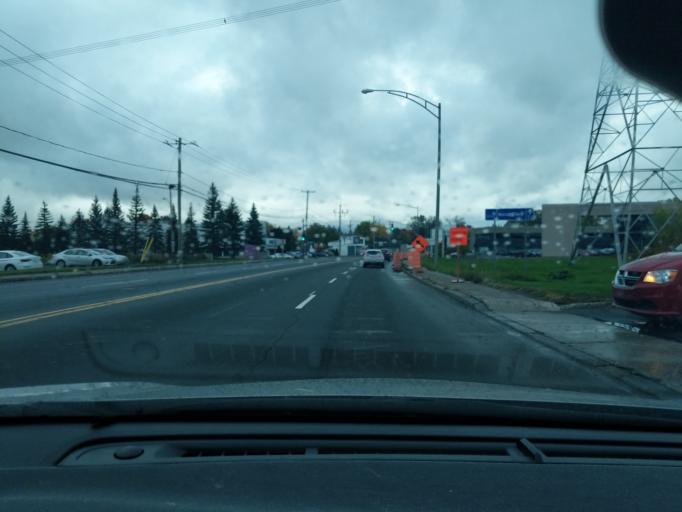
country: CA
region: Quebec
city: L'Ancienne-Lorette
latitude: 46.8054
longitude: -71.3246
